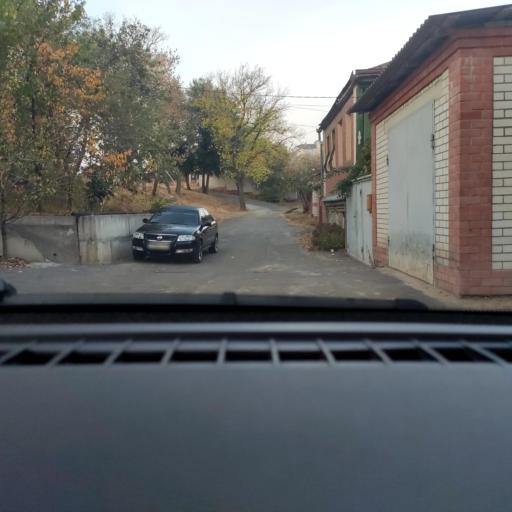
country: RU
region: Voronezj
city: Voronezh
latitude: 51.6657
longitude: 39.2172
